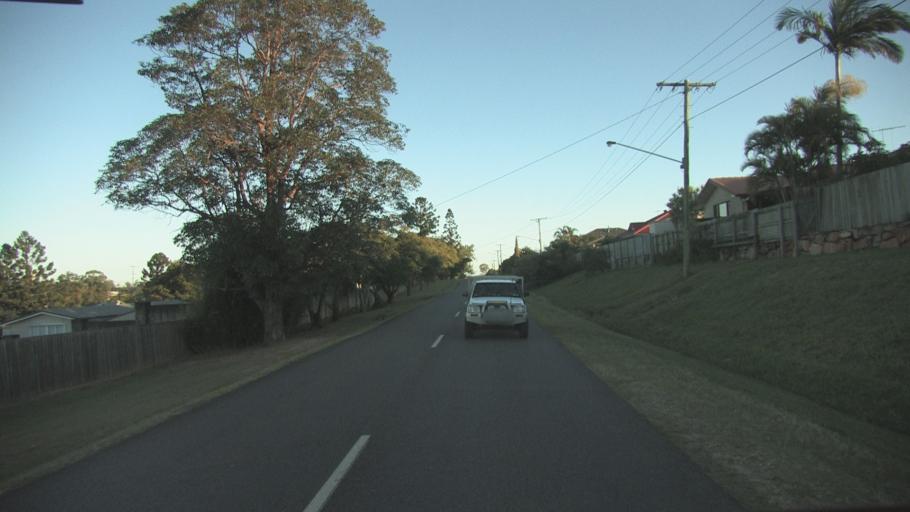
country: AU
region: Queensland
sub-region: Logan
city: Rochedale South
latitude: -27.6046
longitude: 153.1037
